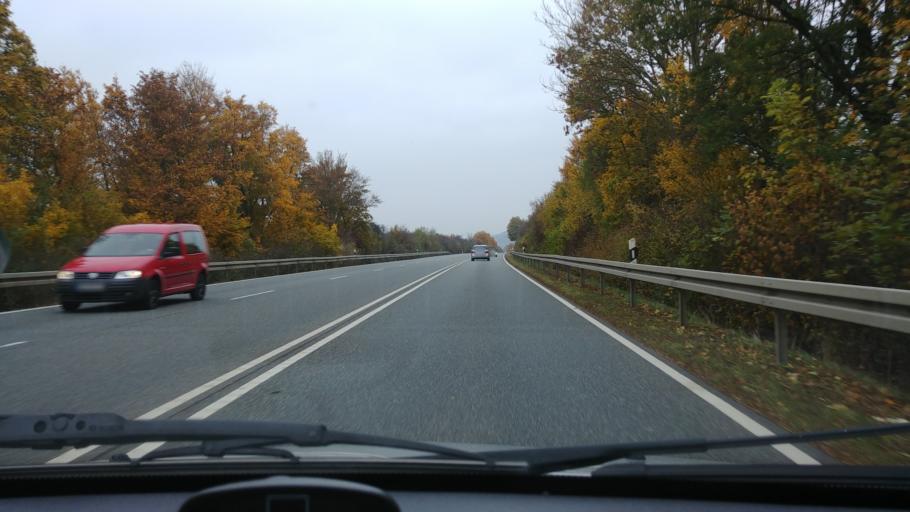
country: DE
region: Hesse
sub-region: Regierungsbezirk Giessen
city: Dehrn
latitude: 50.4487
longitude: 8.0887
